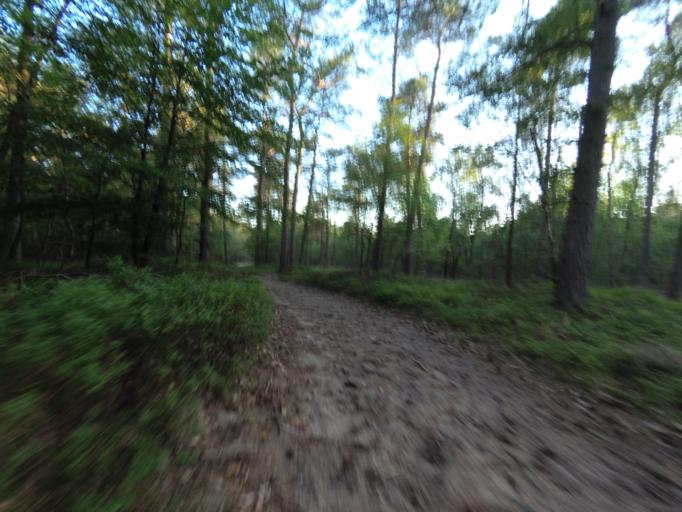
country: NL
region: Gelderland
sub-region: Gemeente Apeldoorn
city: Beekbergen
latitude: 52.1368
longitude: 5.8976
